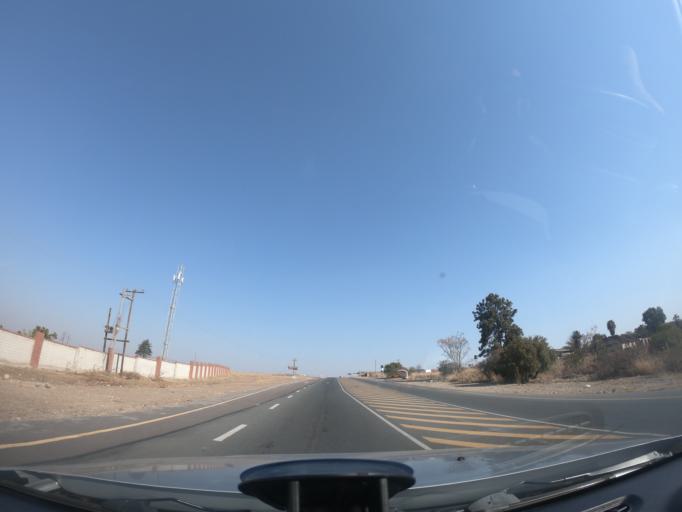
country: ZA
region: Gauteng
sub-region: City of Johannesburg Metropolitan Municipality
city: Diepsloot
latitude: -25.8808
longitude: 28.0277
